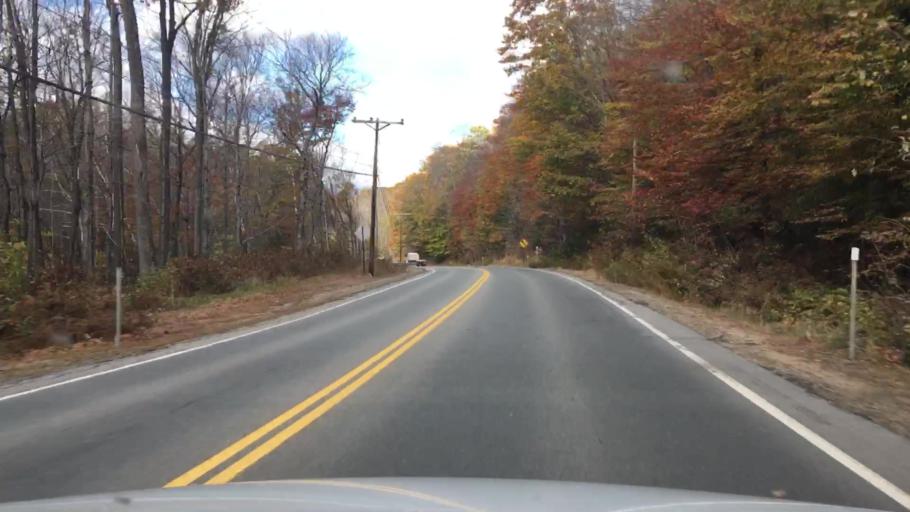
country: US
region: New Hampshire
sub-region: Carroll County
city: North Conway
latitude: 44.1764
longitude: -71.2241
